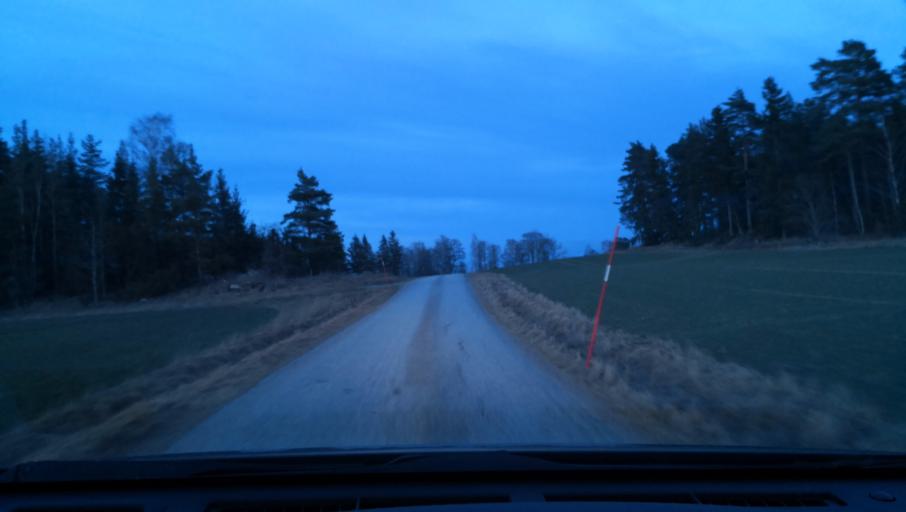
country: SE
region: Uppsala
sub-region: Enkopings Kommun
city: Dalby
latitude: 59.5431
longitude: 17.3603
